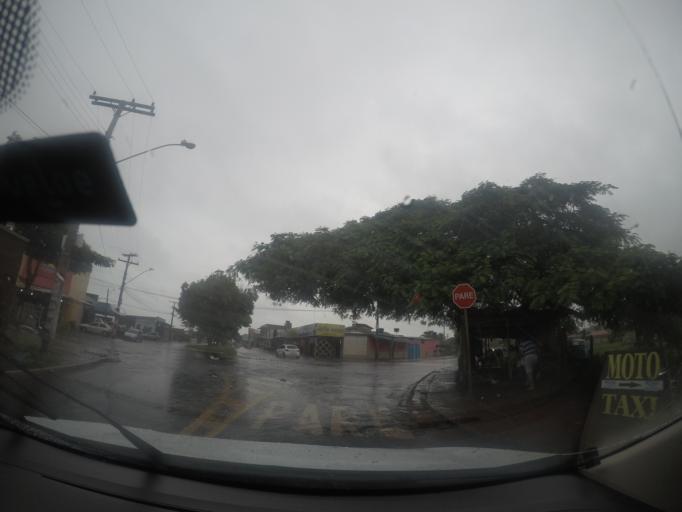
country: BR
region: Goias
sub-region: Goiania
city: Goiania
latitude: -16.6076
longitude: -49.3475
